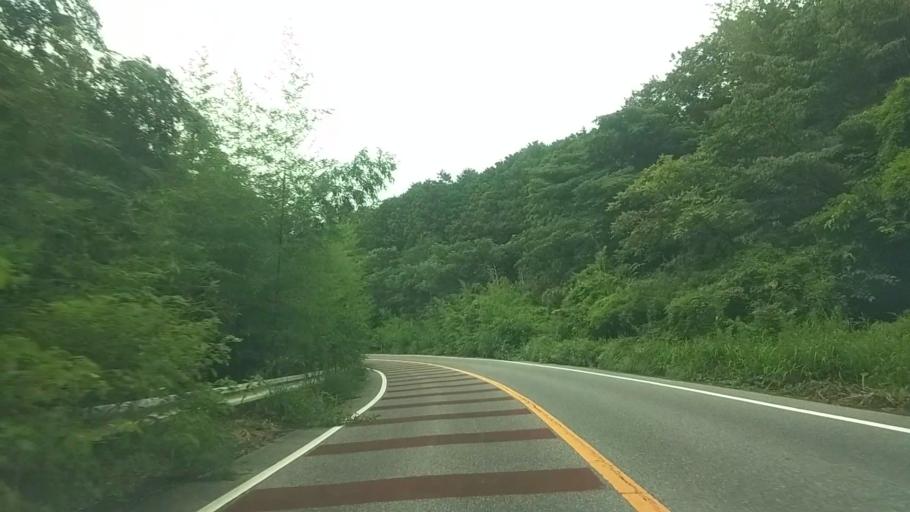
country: JP
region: Chiba
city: Kimitsu
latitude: 35.2379
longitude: 140.0068
